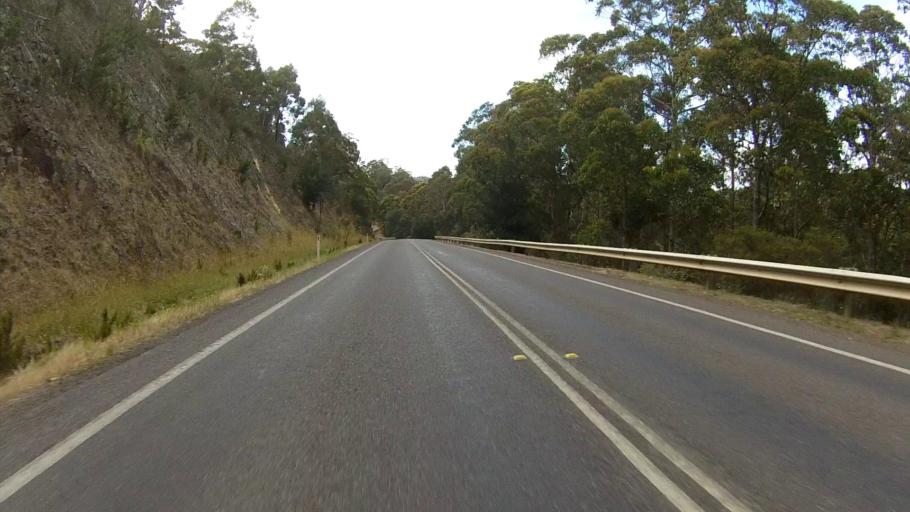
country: AU
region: Tasmania
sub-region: Kingborough
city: Kettering
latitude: -43.0992
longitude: 147.2425
